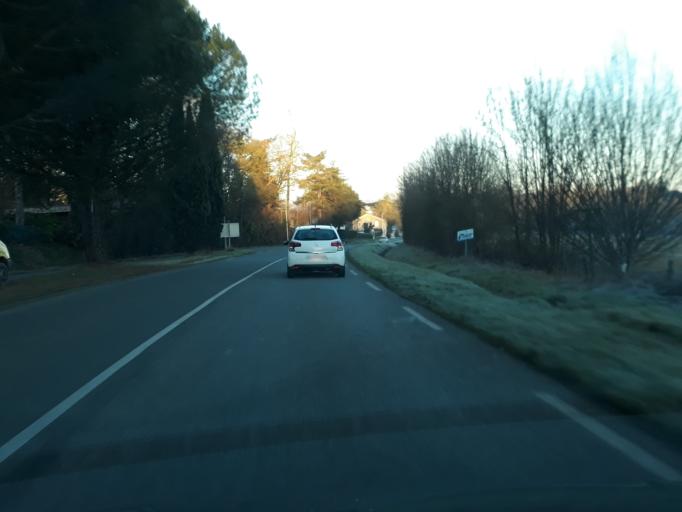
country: FR
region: Midi-Pyrenees
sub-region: Departement du Gers
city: Auch
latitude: 43.6360
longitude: 0.6063
